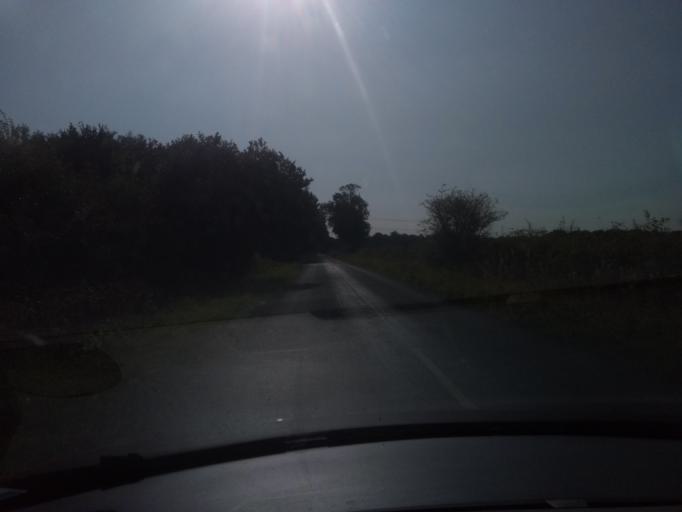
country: GB
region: England
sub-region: North Yorkshire
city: Camblesforth
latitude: 53.7403
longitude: -1.0382
